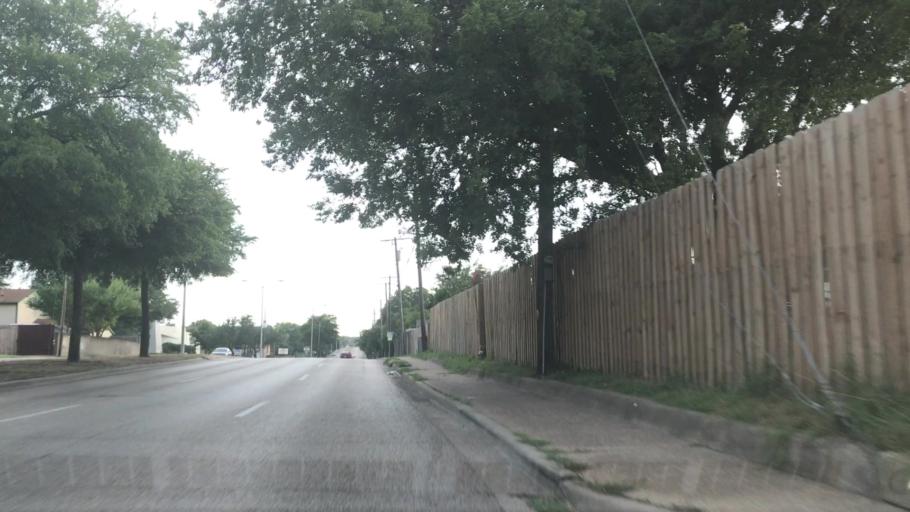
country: US
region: Texas
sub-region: Dallas County
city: Mesquite
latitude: 32.8323
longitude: -96.6359
